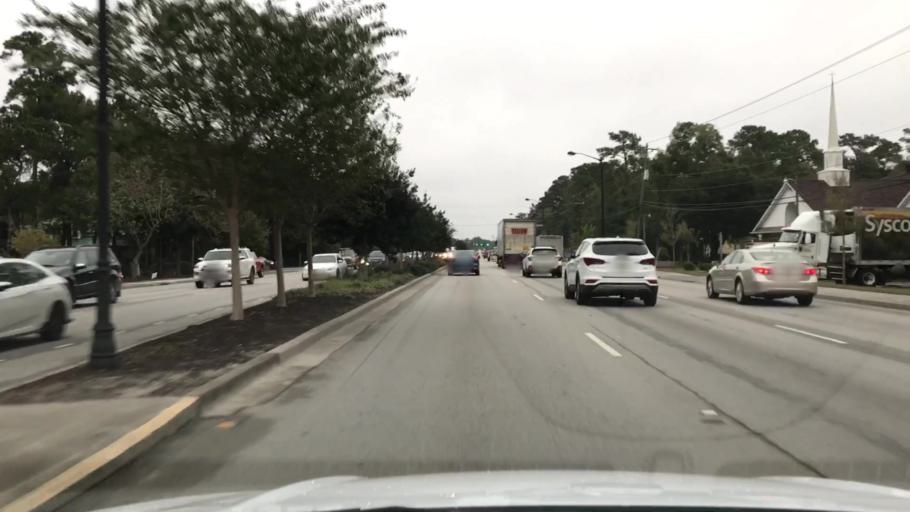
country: US
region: South Carolina
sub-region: Charleston County
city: Isle of Palms
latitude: 32.8515
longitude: -79.8053
